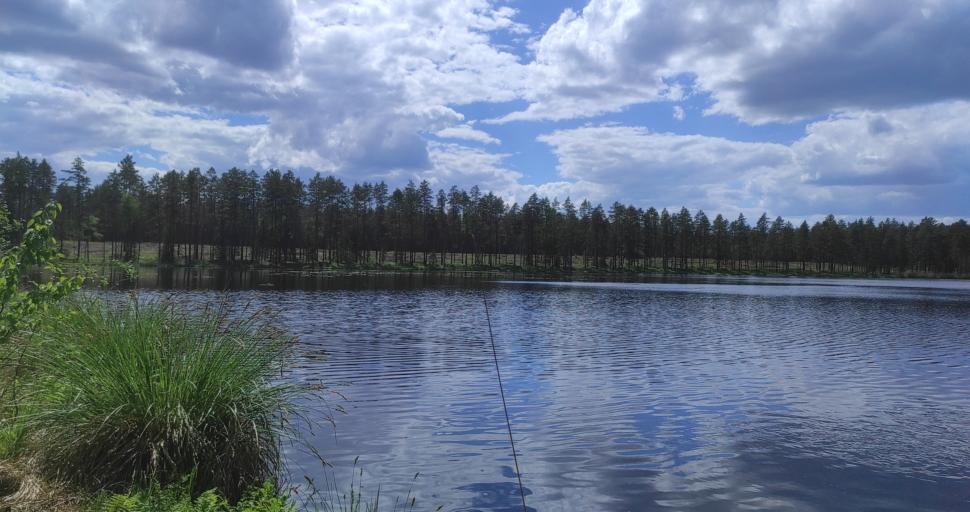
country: LV
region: Talsu Rajons
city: Stende
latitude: 57.1257
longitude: 22.3442
